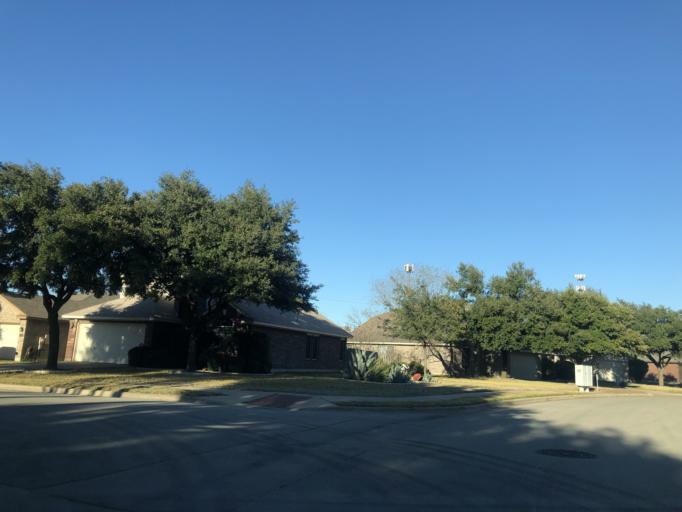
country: US
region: Texas
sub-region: Travis County
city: Windemere
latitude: 30.4811
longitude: -97.6574
